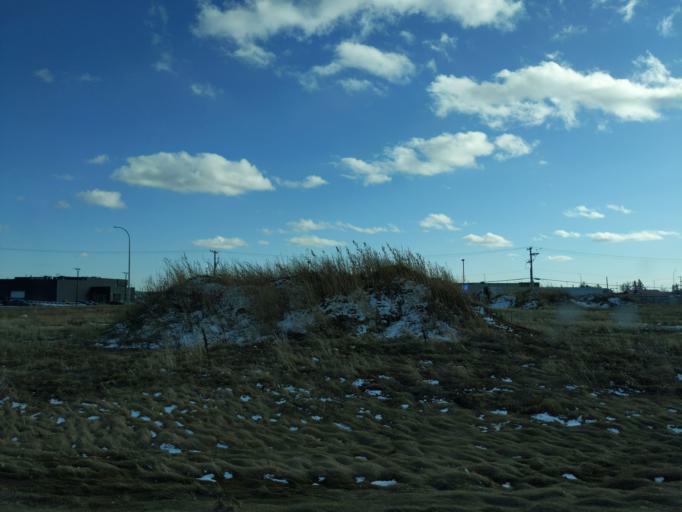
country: CA
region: Saskatchewan
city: Lloydminster
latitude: 53.2802
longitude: -109.9767
